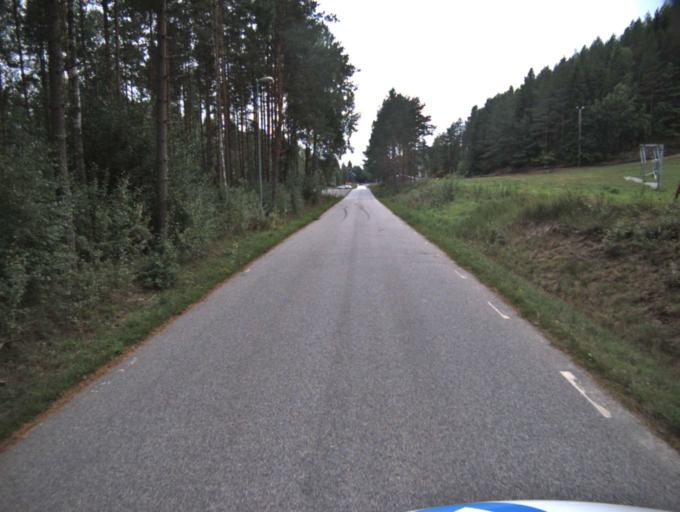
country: SE
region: Vaestra Goetaland
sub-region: Ulricehamns Kommun
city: Ulricehamn
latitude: 57.8222
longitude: 13.4148
